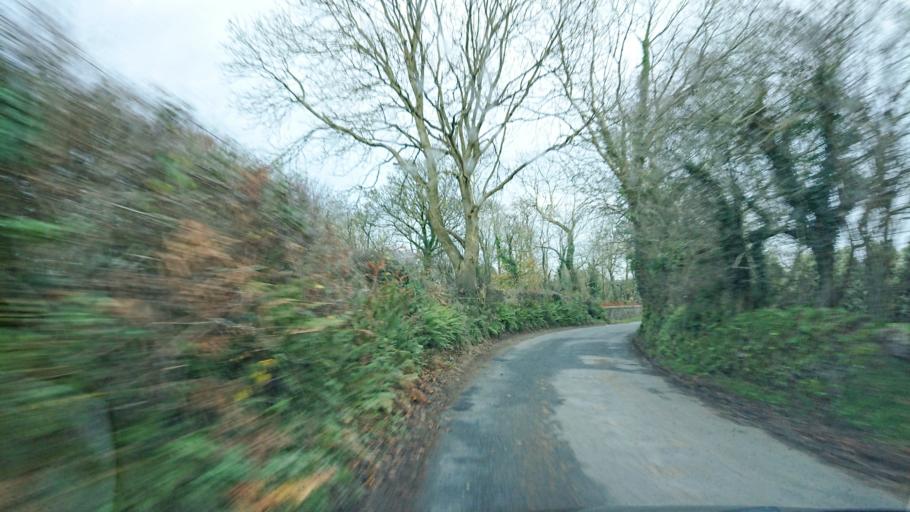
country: IE
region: Munster
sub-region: Waterford
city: Dunmore East
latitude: 52.2466
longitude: -7.0000
